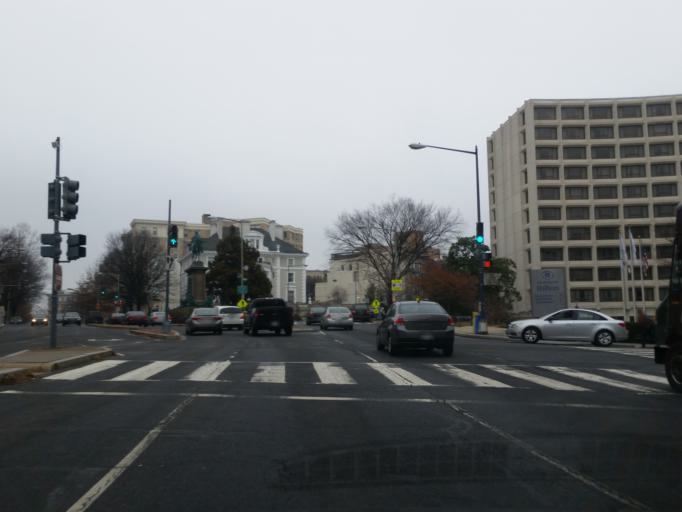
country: US
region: Washington, D.C.
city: Washington, D.C.
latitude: 38.9158
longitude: -77.0463
